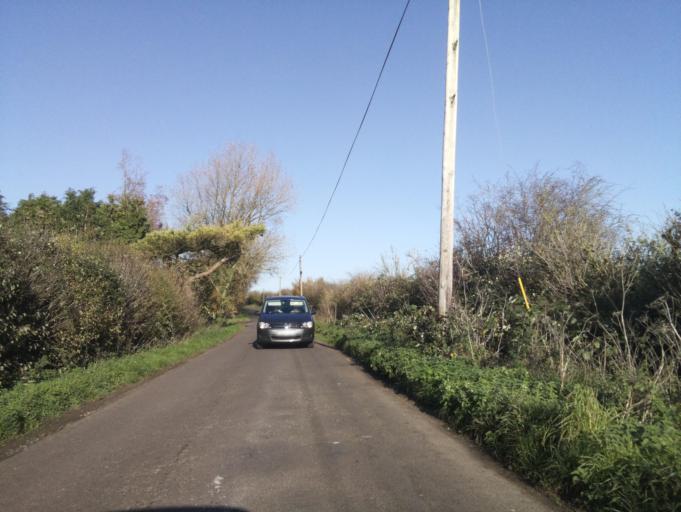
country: GB
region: England
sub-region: Dorset
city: Sherborne
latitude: 50.9994
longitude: -2.5118
